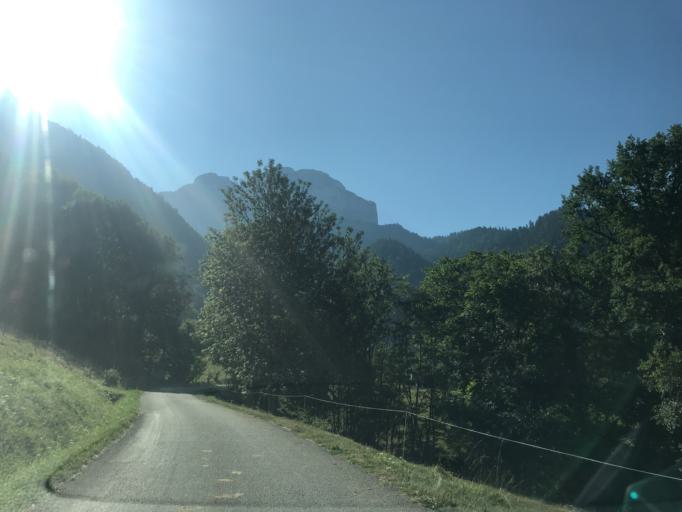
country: FR
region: Rhone-Alpes
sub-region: Departement de la Haute-Savoie
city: Villaz
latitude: 45.9615
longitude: 6.2175
